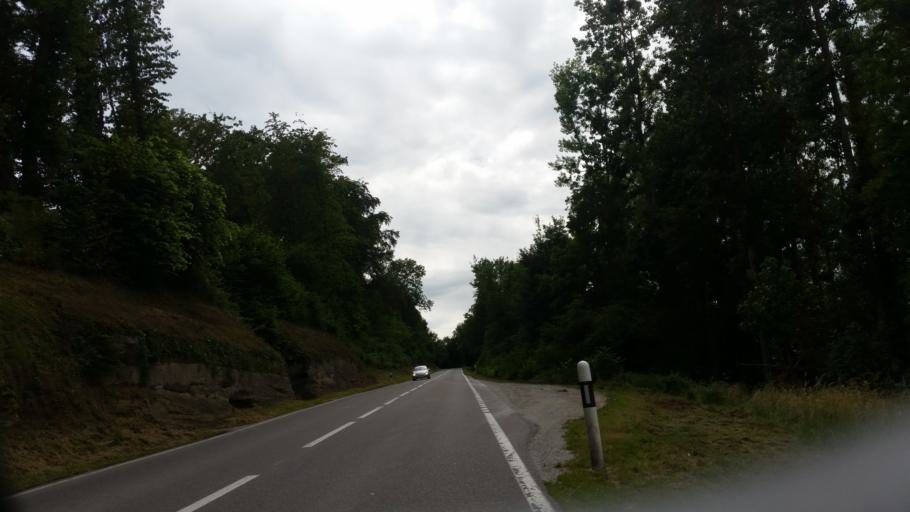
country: CH
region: Fribourg
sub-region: Broye District
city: Estavayer-le-Lac
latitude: 46.8300
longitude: 6.8099
